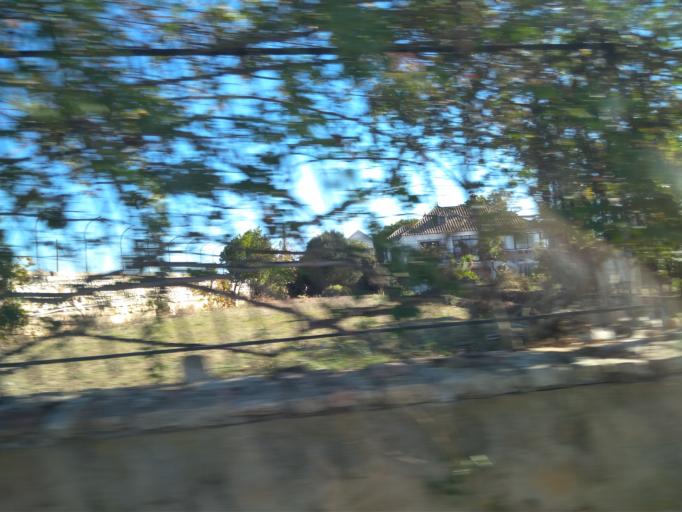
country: PT
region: Faro
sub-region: Faro
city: Faro
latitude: 37.0558
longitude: -7.9544
